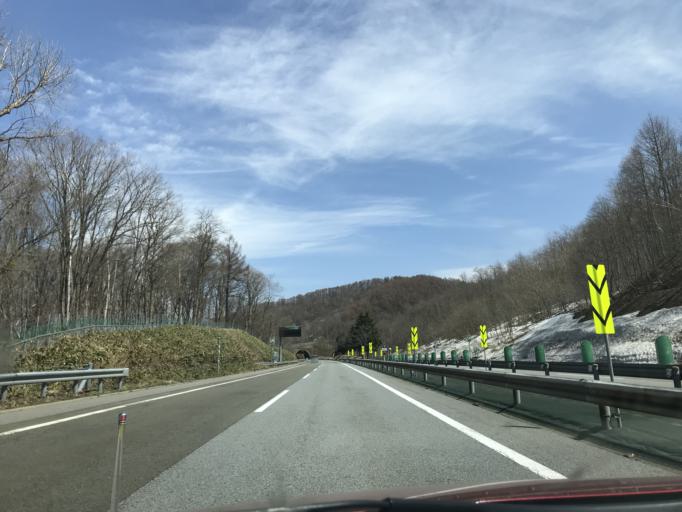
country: JP
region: Hokkaido
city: Bibai
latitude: 43.2971
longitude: 141.8716
